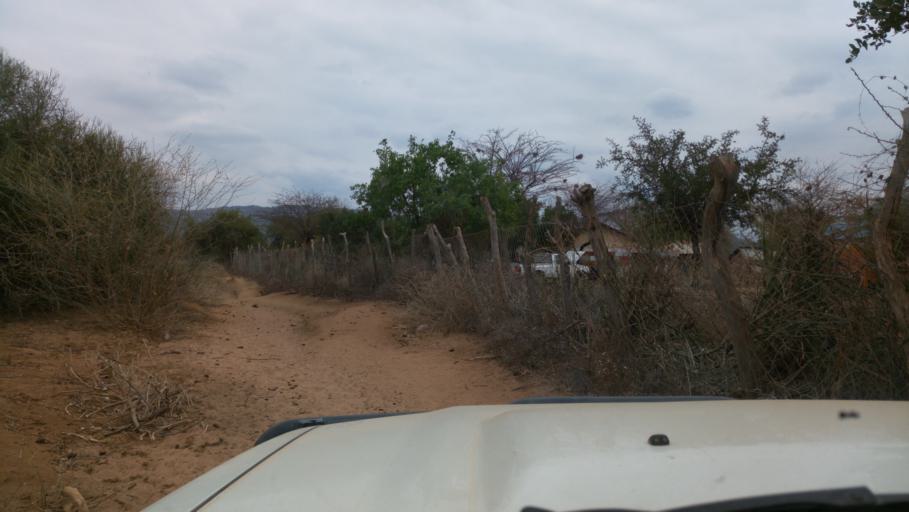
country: KE
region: Kitui
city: Kitui
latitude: -1.3576
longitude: 38.2288
